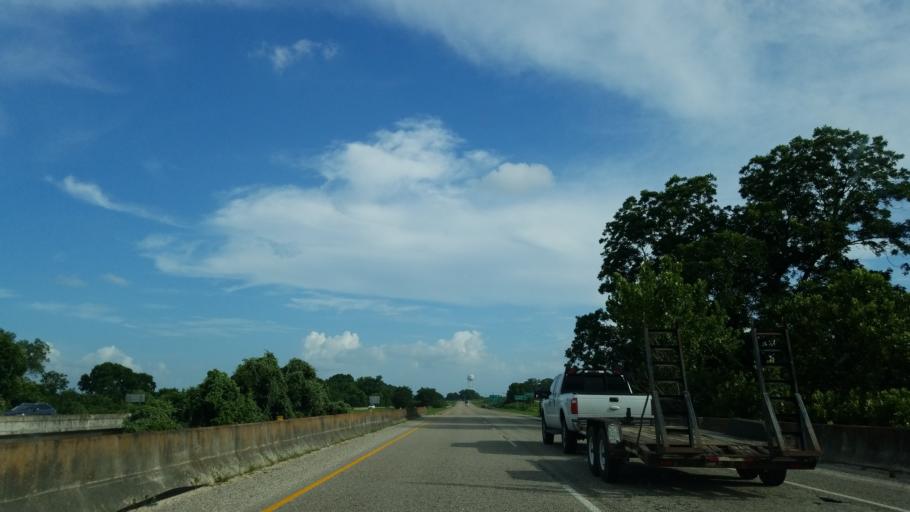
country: US
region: Texas
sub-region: Colorado County
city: Columbus
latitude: 29.7194
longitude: -96.5801
